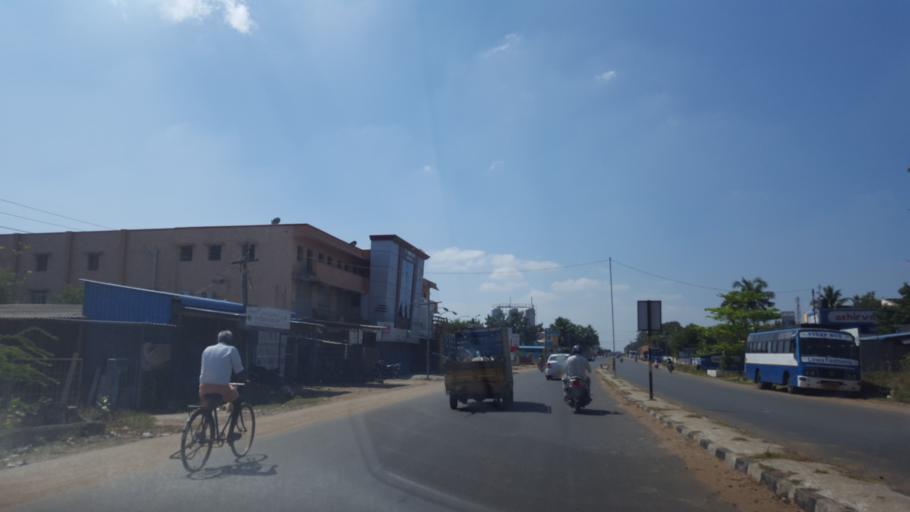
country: IN
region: Tamil Nadu
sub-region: Kancheepuram
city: Karumbakkam
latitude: 12.7181
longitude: 80.1887
